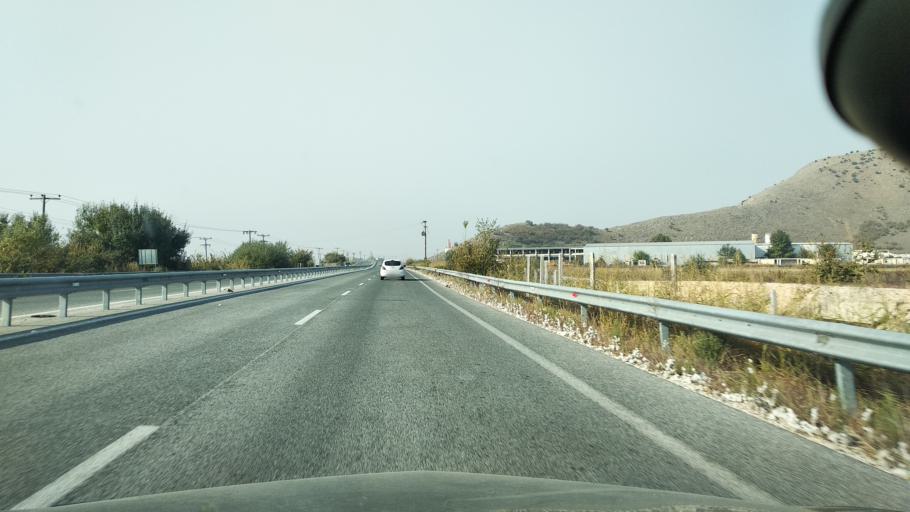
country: GR
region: Thessaly
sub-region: Trikala
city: Oichalia
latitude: 39.5665
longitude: 21.9768
